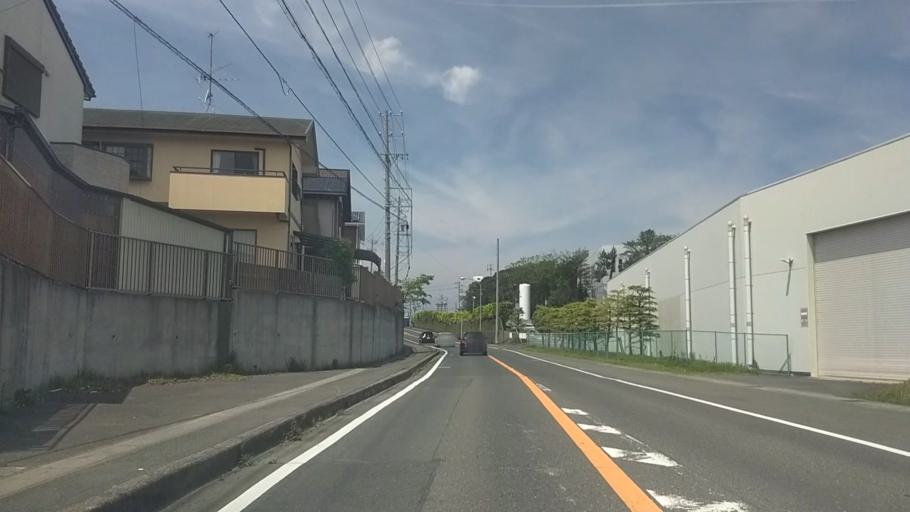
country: JP
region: Shizuoka
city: Kosai-shi
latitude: 34.7086
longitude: 137.5492
